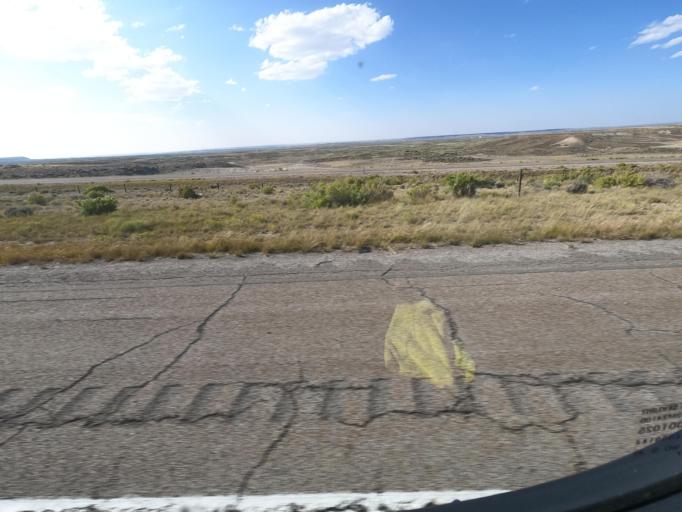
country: US
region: Wyoming
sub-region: Uinta County
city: Lyman
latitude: 41.5198
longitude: -109.9657
